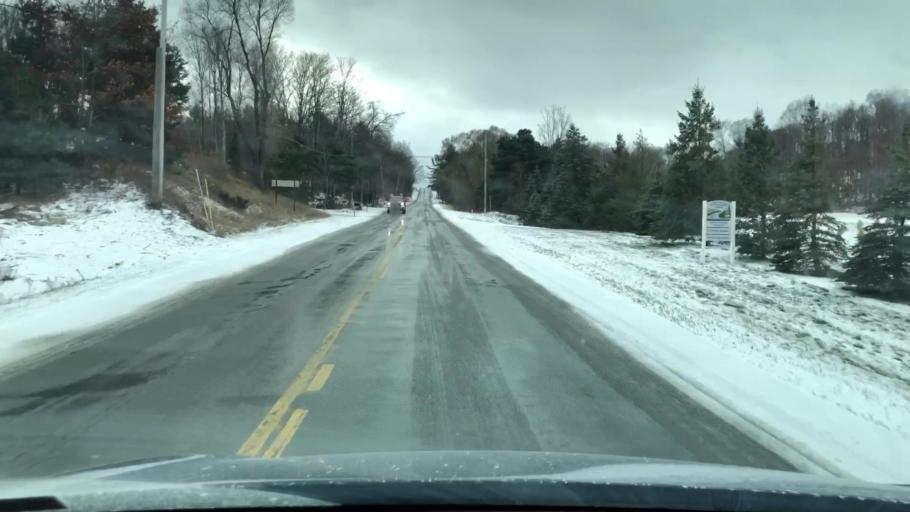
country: US
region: Michigan
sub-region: Antrim County
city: Elk Rapids
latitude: 44.8921
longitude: -85.5154
